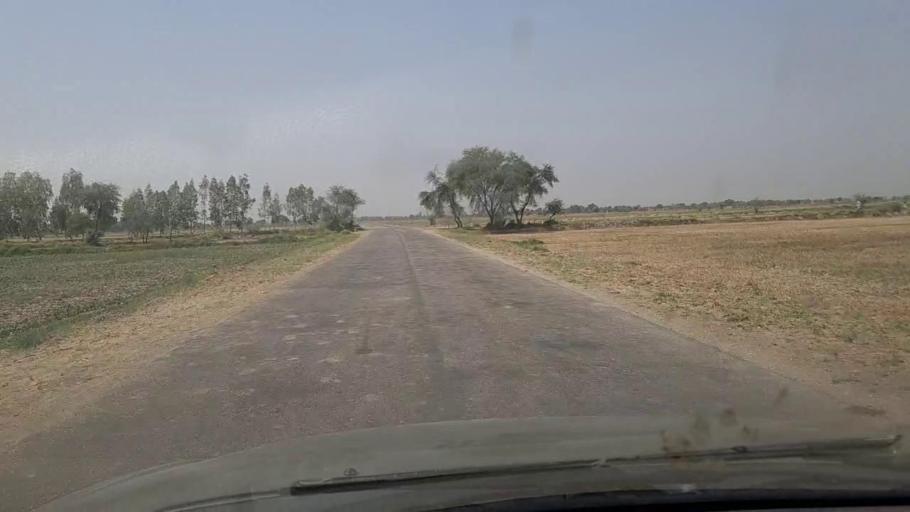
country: PK
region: Sindh
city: Khanpur
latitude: 27.8635
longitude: 69.4399
